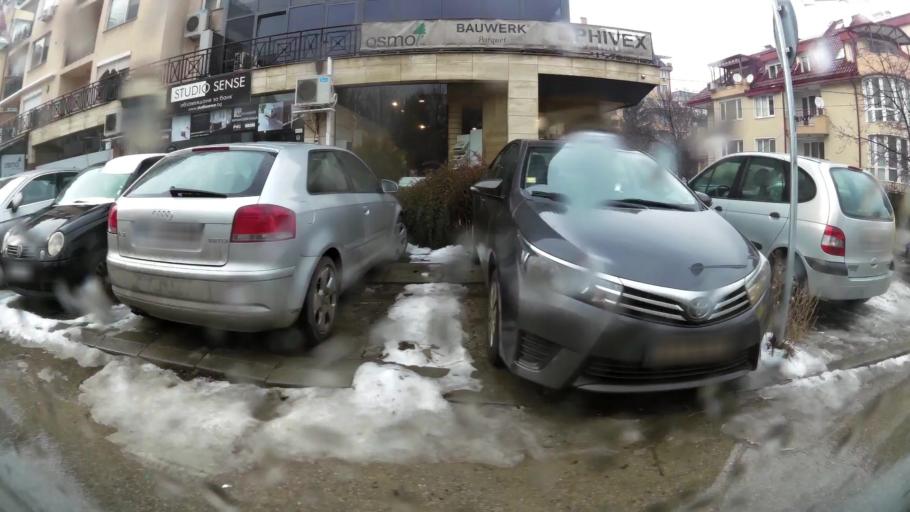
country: BG
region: Sofia-Capital
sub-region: Stolichna Obshtina
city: Sofia
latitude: 42.6635
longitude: 23.2857
